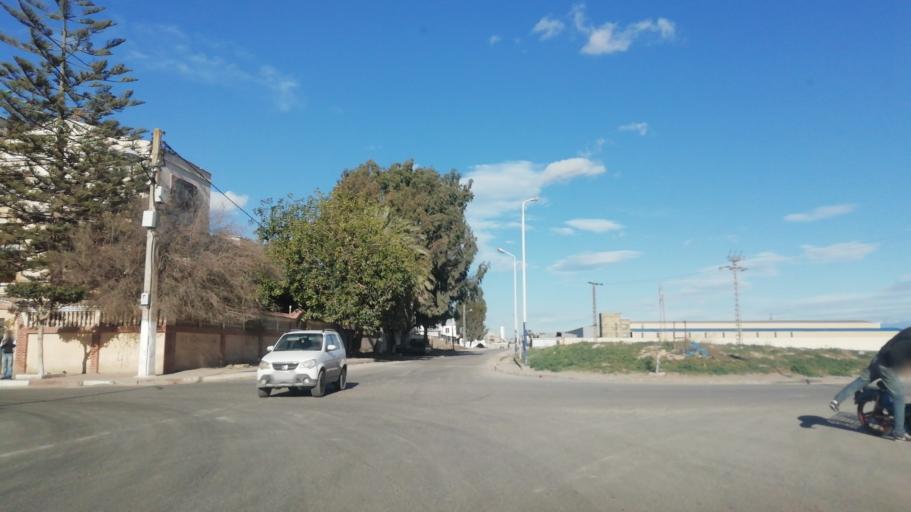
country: DZ
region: Oran
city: Sidi ech Chahmi
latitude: 35.6372
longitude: -0.5490
